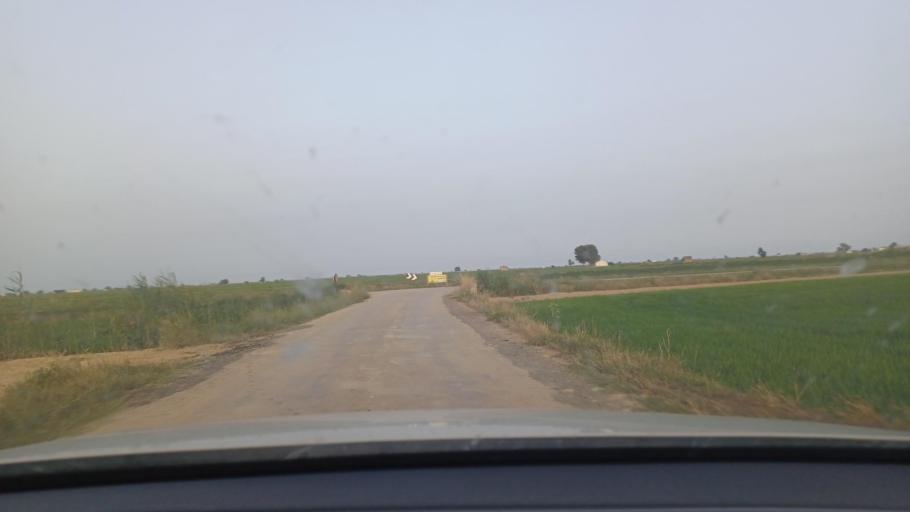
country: ES
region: Catalonia
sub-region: Provincia de Tarragona
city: Amposta
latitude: 40.7000
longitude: 0.6441
